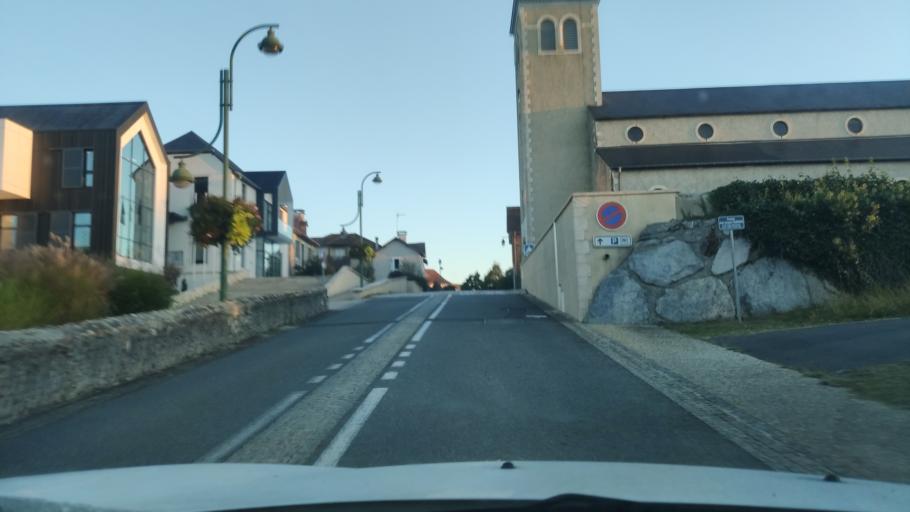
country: FR
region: Aquitaine
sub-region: Departement des Pyrenees-Atlantiques
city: Sauvagnon
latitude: 43.4026
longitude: -0.3870
